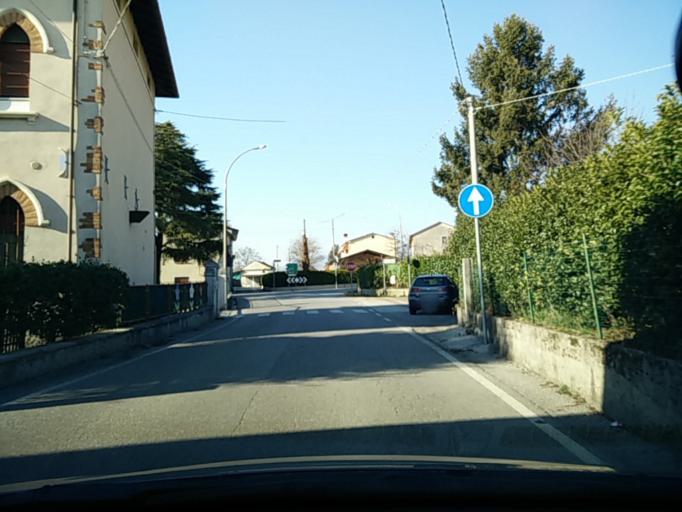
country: IT
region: Veneto
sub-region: Provincia di Treviso
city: Sarmede
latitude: 45.9762
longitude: 12.3870
